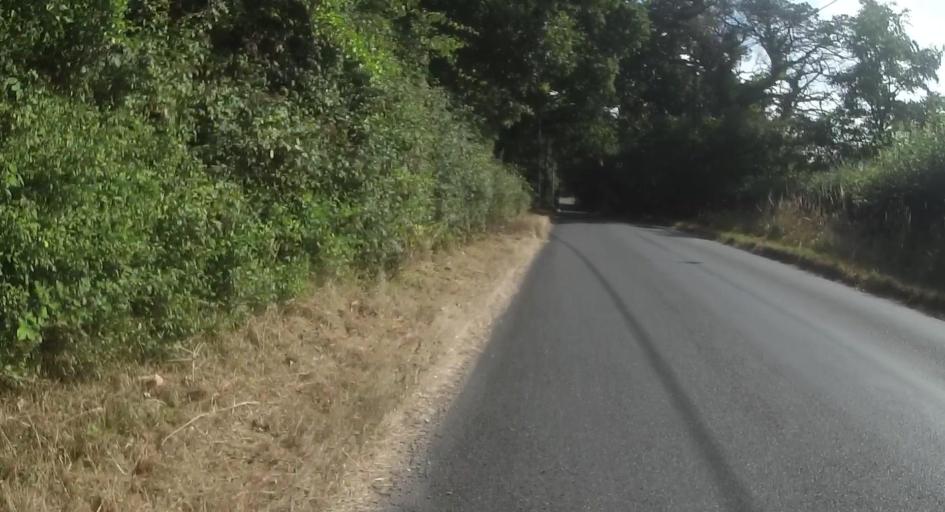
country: GB
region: England
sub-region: Dorset
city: Wareham
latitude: 50.6697
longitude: -2.1138
